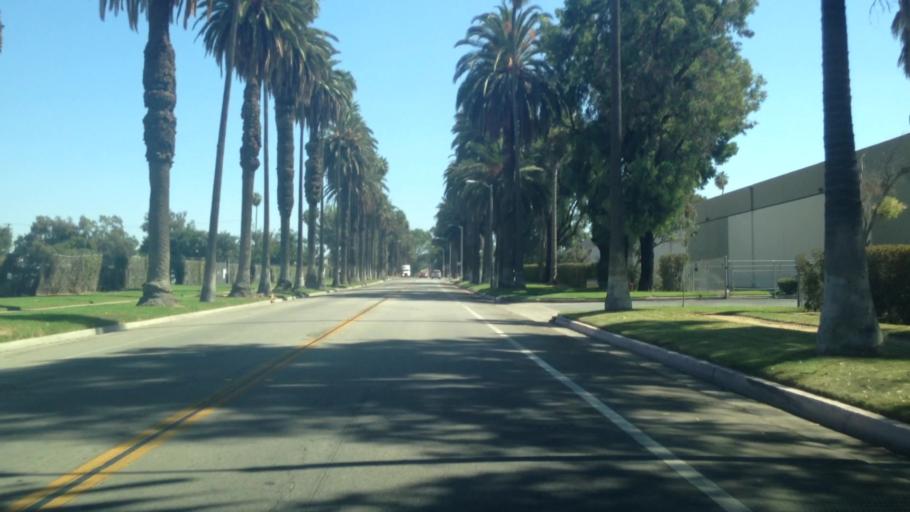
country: US
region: California
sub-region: Riverside County
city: Riverside
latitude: 33.9266
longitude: -117.4082
